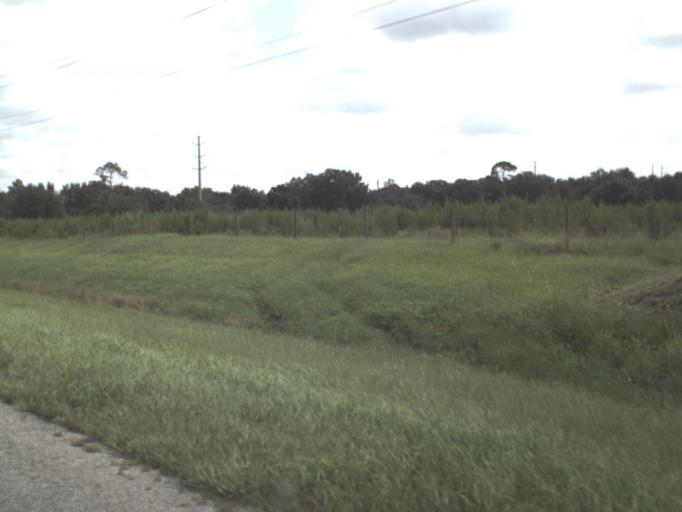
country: US
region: Florida
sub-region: DeSoto County
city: Arcadia
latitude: 27.3129
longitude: -81.8174
